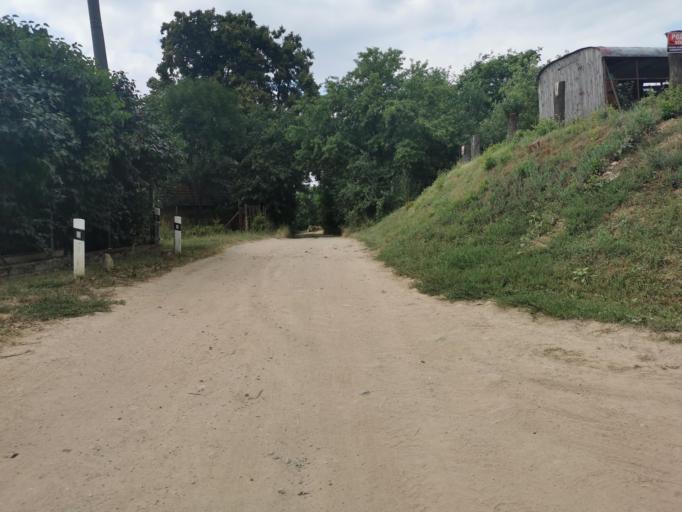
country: SK
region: Nitriansky
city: Brezova pod Bradlom
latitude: 48.6967
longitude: 17.5048
